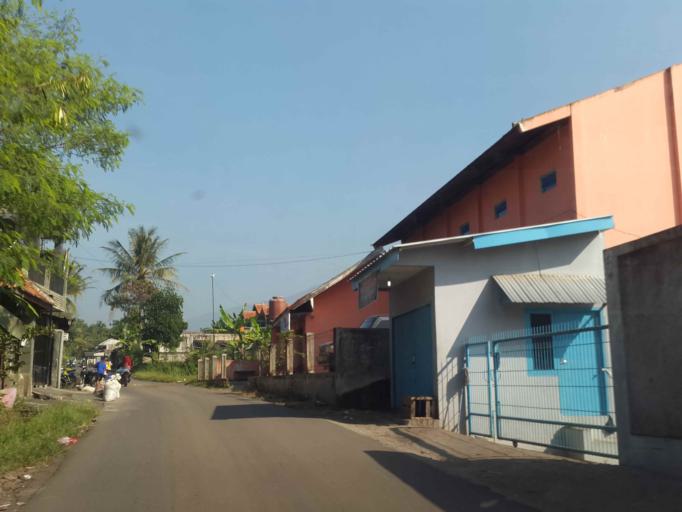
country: ID
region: West Java
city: Cibeber
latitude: -6.8681
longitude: 107.0925
